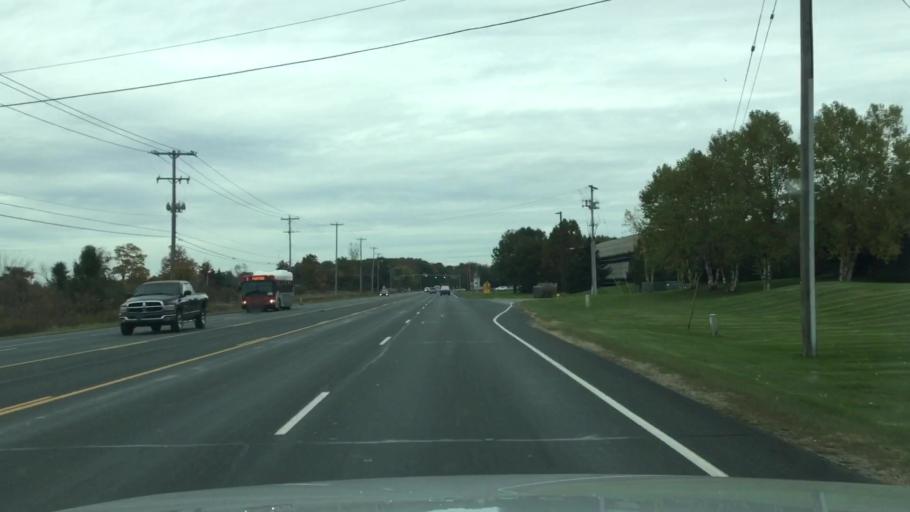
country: US
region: Michigan
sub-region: Kalamazoo County
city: Portage
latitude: 42.2271
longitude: -85.5404
